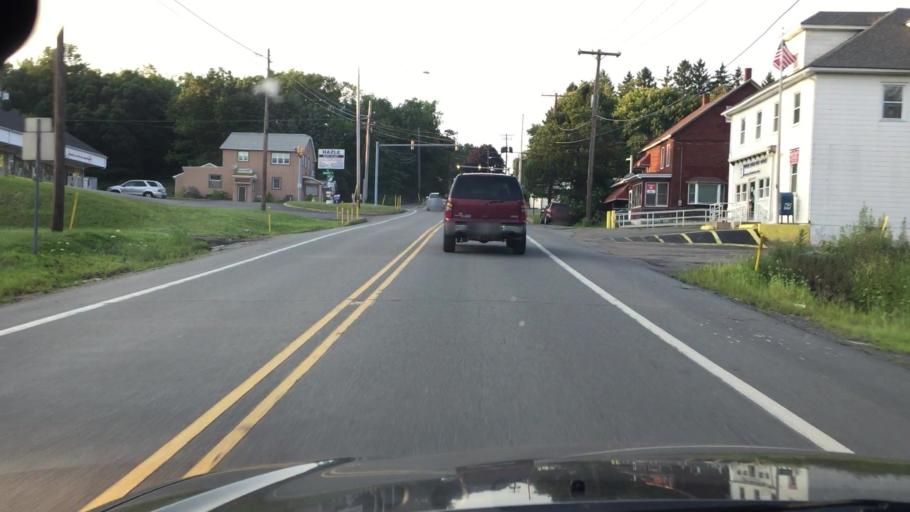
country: US
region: Pennsylvania
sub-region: Luzerne County
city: Harleigh
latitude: 40.9797
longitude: -75.9757
